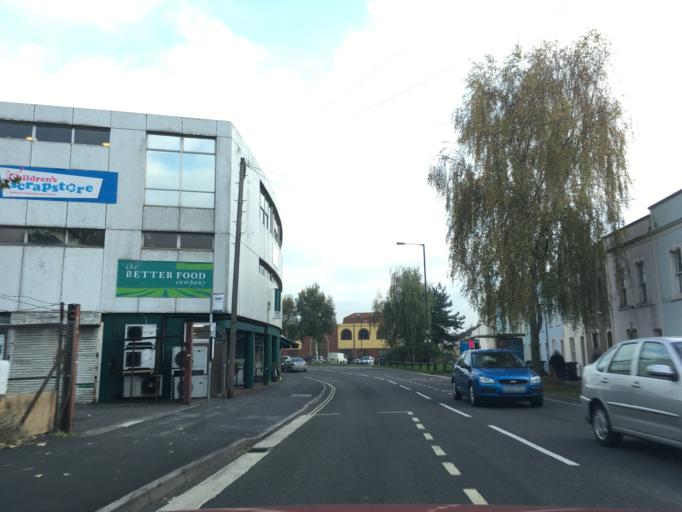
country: GB
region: England
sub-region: Bristol
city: Bristol
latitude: 51.4686
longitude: -2.5790
